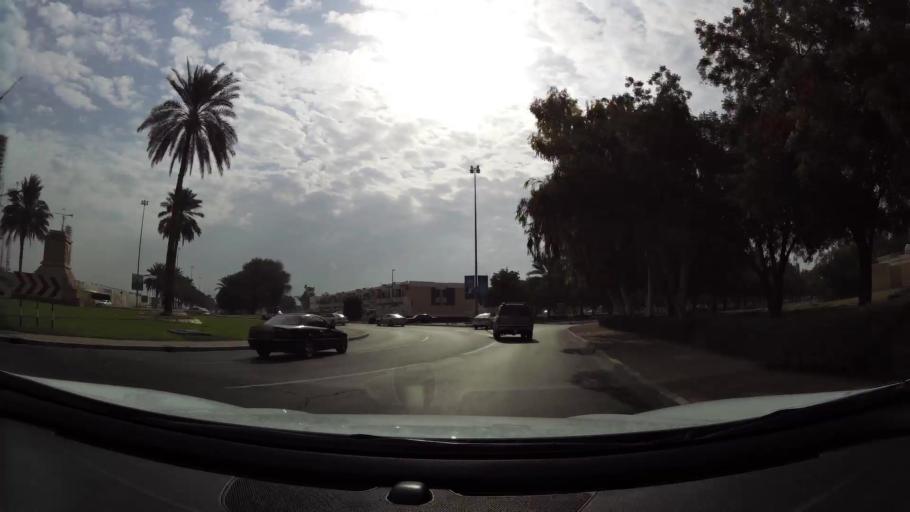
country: AE
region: Abu Dhabi
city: Al Ain
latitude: 24.2242
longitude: 55.7444
